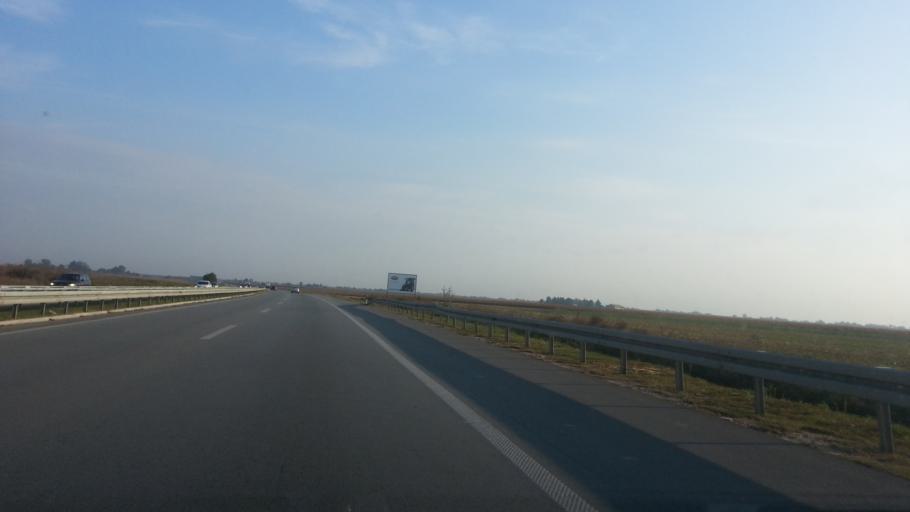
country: RS
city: Novi Banovci
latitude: 44.9028
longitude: 20.3036
